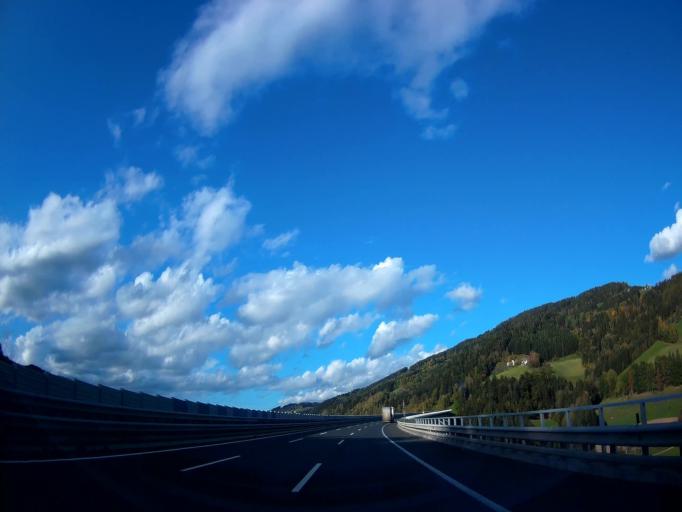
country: AT
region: Carinthia
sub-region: Politischer Bezirk Wolfsberg
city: Wolfsberg
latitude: 46.8604
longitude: 14.8346
